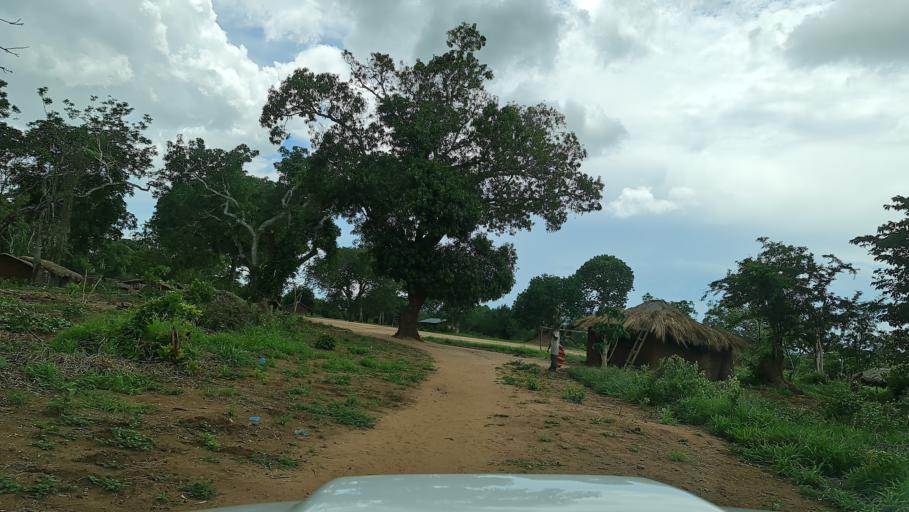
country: MZ
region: Nampula
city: Ilha de Mocambique
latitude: -15.4971
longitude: 40.1602
